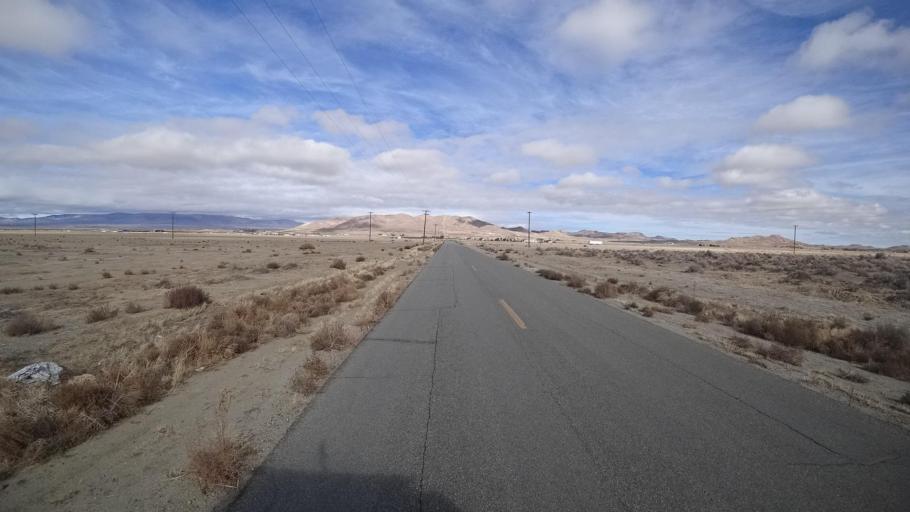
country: US
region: California
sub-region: Kern County
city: Rosamond
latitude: 34.8481
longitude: -118.2732
